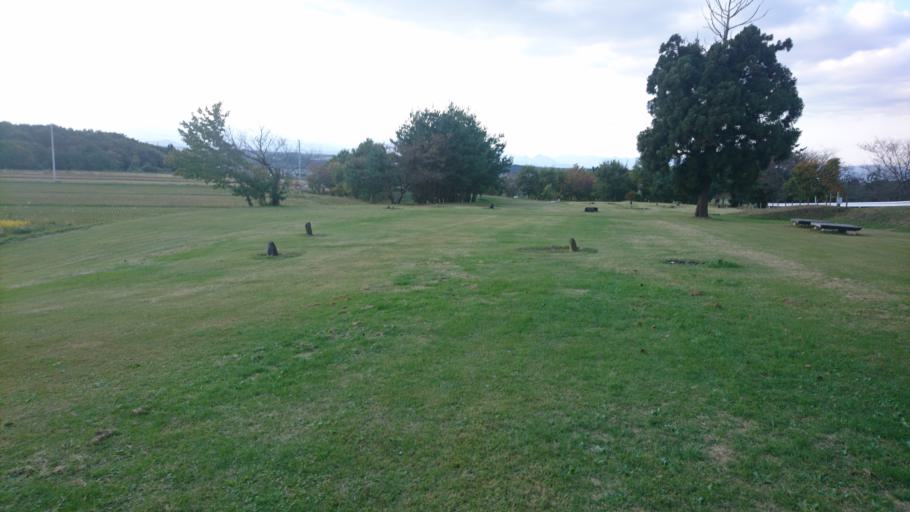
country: JP
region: Iwate
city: Kitakami
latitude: 39.2415
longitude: 141.1319
